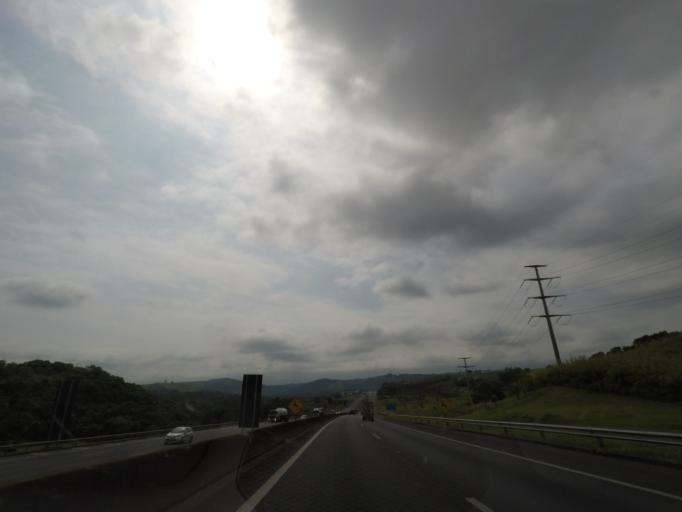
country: BR
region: Sao Paulo
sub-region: Valinhos
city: Valinhos
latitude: -22.9025
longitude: -46.9824
